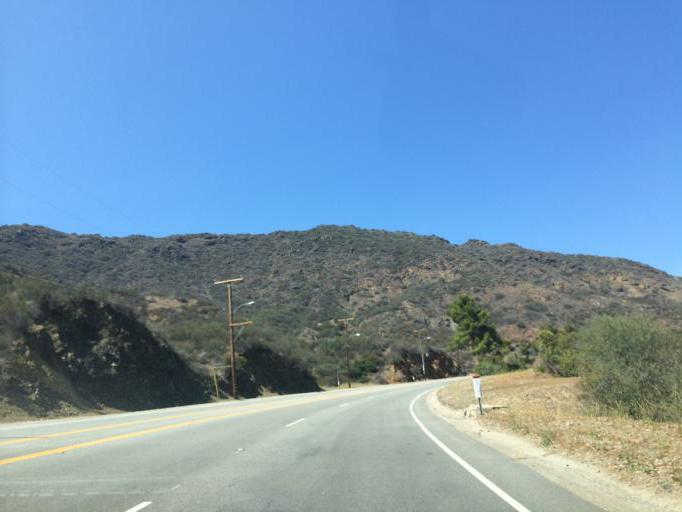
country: US
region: California
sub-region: Los Angeles County
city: Agoura Hills
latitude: 34.1280
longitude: -118.7768
